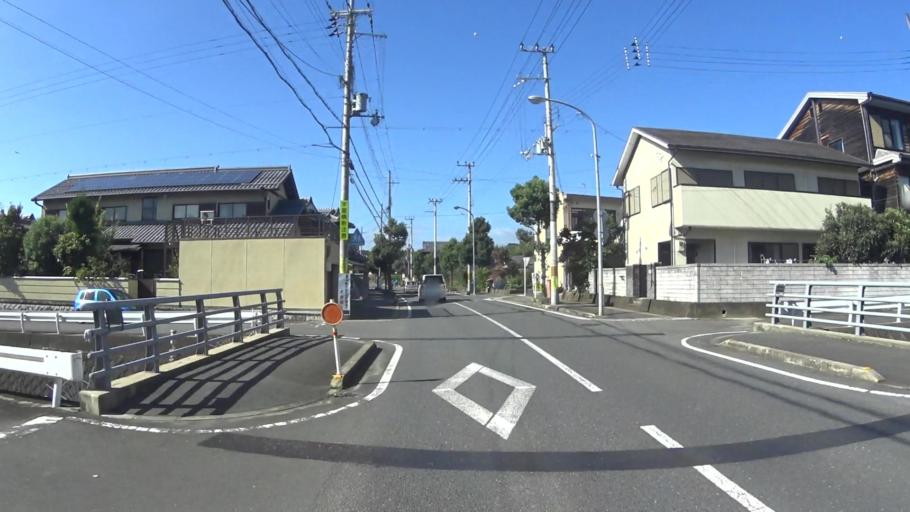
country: JP
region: Kyoto
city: Kameoka
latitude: 35.0253
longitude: 135.5876
